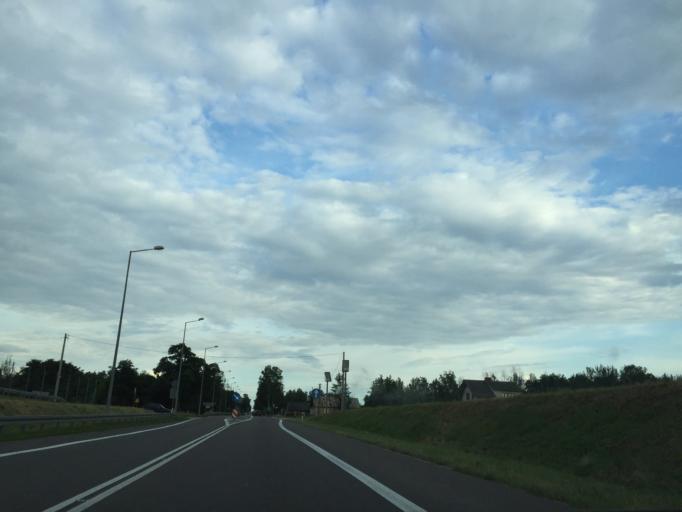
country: PL
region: Lublin Voivodeship
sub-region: Powiat lubartowski
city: Kock
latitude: 51.5997
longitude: 22.4730
